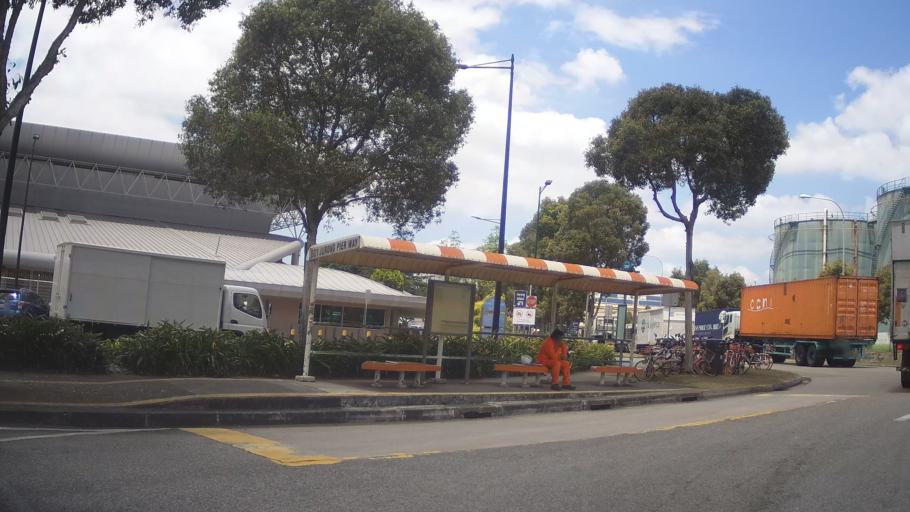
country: SG
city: Singapore
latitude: 1.3101
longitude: 103.7115
